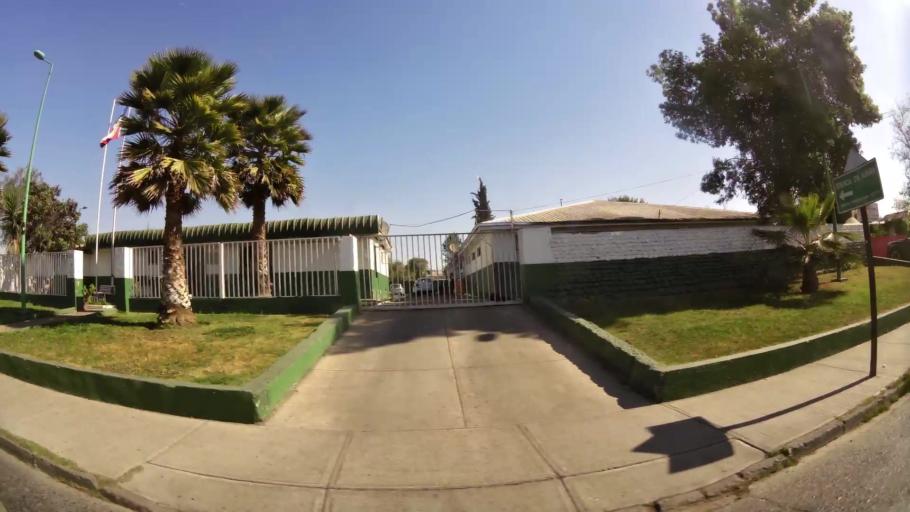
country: CL
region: Santiago Metropolitan
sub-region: Provincia de Santiago
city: Santiago
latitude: -33.5080
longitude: -70.6789
